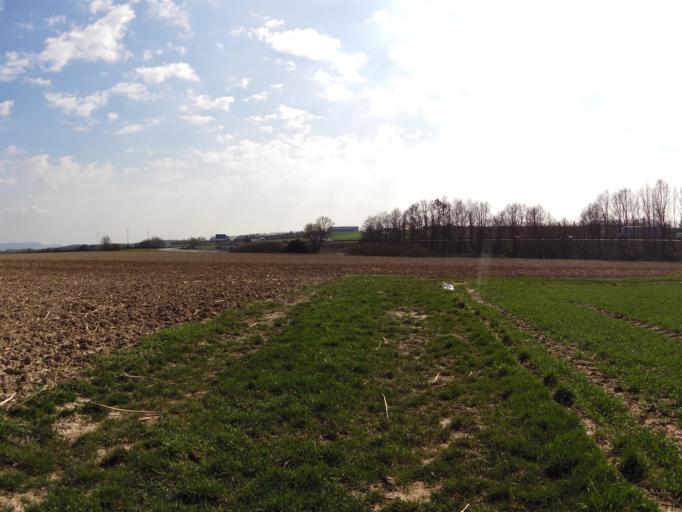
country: DE
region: Bavaria
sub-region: Regierungsbezirk Unterfranken
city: Rottendorf
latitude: 49.7938
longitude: 10.0619
